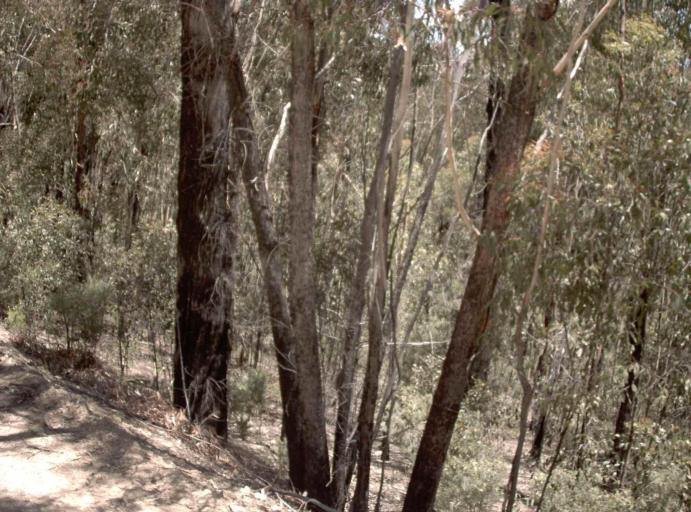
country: AU
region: New South Wales
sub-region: Snowy River
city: Jindabyne
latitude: -37.0823
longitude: 148.3295
